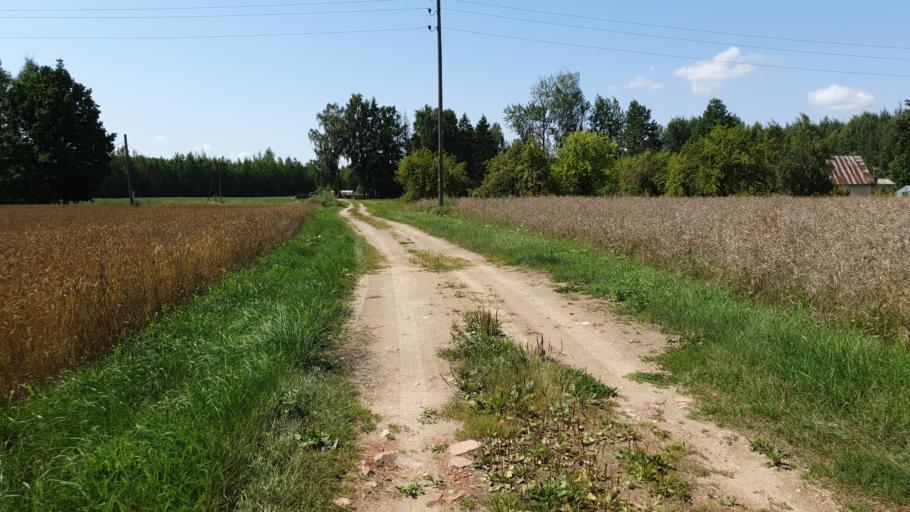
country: LV
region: Bauskas Rajons
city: Bauska
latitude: 56.3295
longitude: 24.4474
